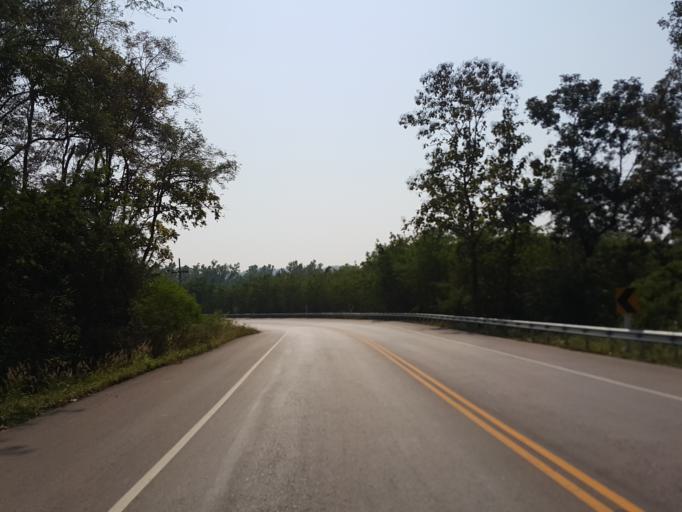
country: TH
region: Lampang
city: Mueang Pan
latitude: 18.8926
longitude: 99.6041
